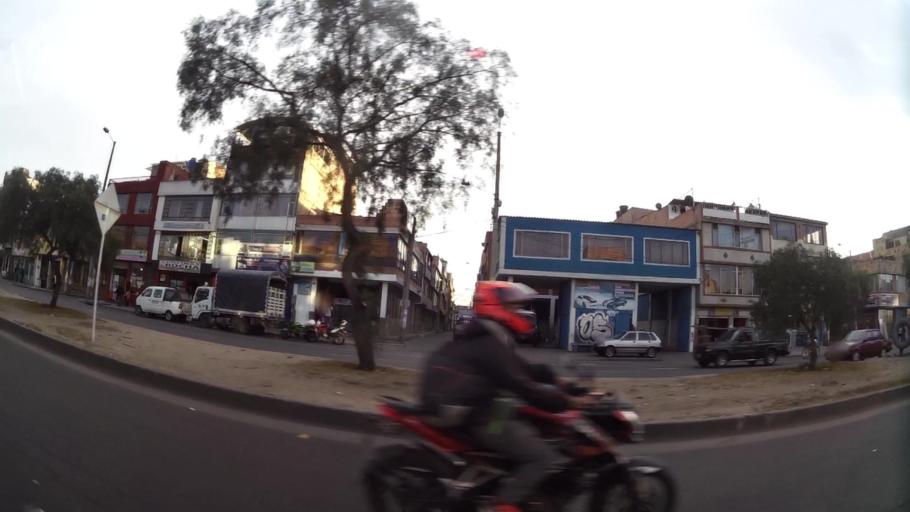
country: CO
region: Cundinamarca
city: Soacha
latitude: 4.6236
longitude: -74.1674
